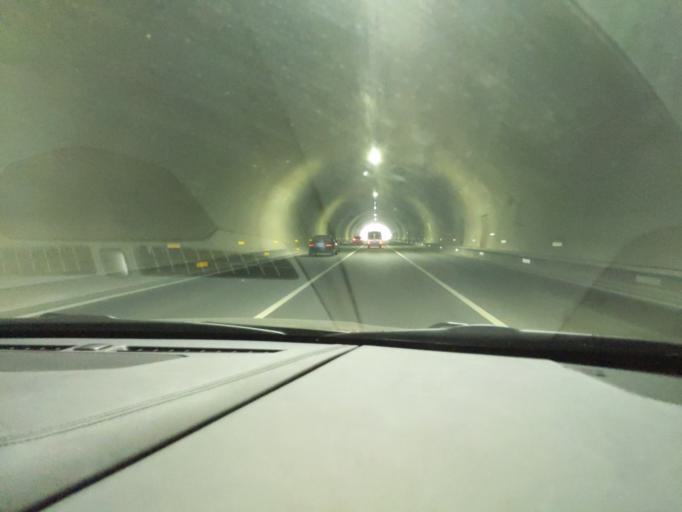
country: CN
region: Fujian
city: Cizao
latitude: 24.7762
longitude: 118.5111
